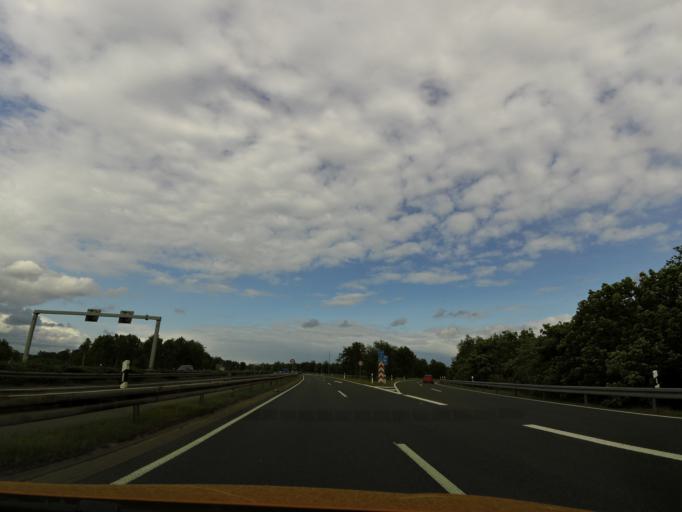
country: DE
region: Lower Saxony
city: Isernhagen Farster Bauerschaft
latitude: 52.4259
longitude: 9.8821
